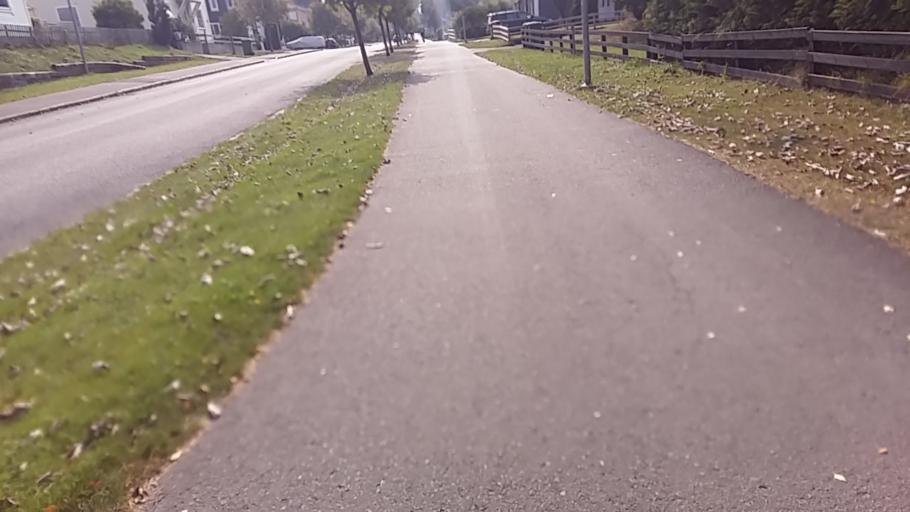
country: SE
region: Joenkoeping
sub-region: Jonkopings Kommun
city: Jonkoping
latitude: 57.7620
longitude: 14.1525
